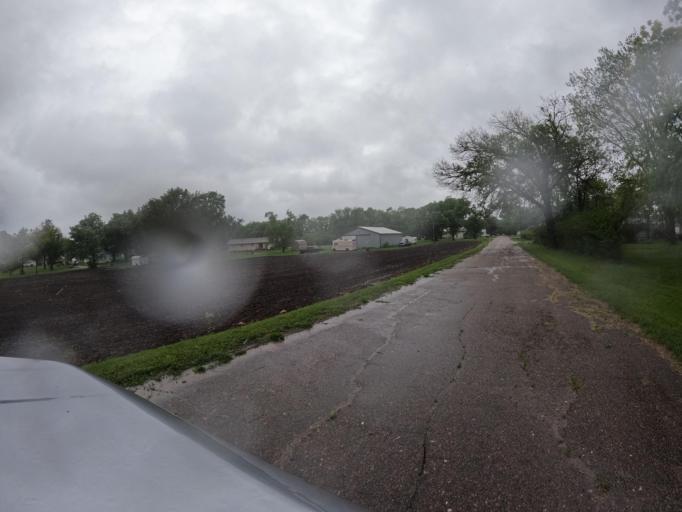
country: US
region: Nebraska
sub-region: Gage County
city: Wymore
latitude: 40.1245
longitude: -96.6545
